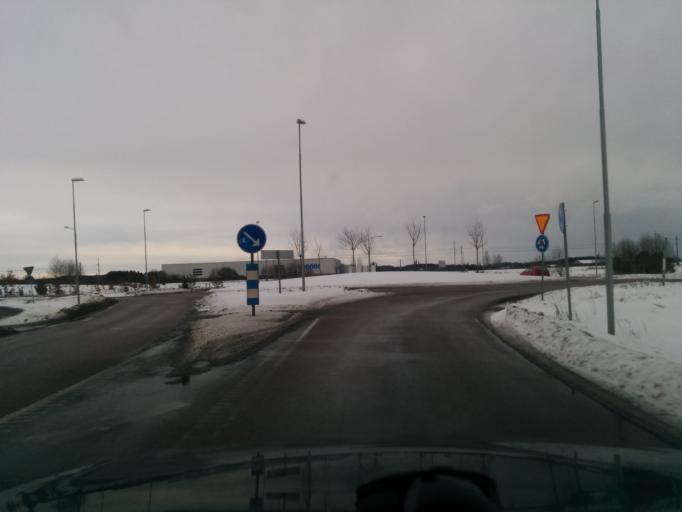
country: SE
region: Vaestmanland
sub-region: Vasteras
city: Vasteras
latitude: 59.5890
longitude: 16.4430
